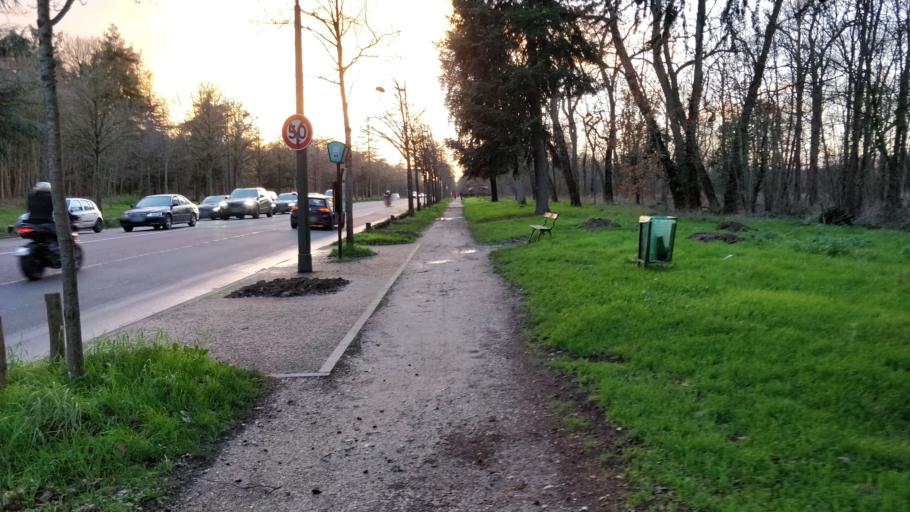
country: FR
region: Ile-de-France
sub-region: Departement des Hauts-de-Seine
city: Neuilly-sur-Seine
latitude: 48.8726
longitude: 2.2642
